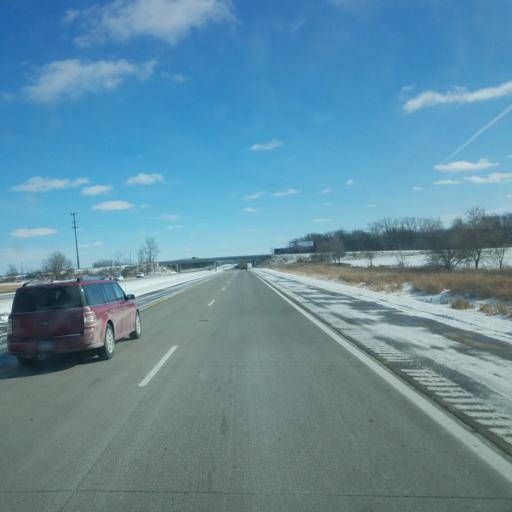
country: US
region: Michigan
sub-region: Ingham County
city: Okemos
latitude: 42.6715
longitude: -84.3673
